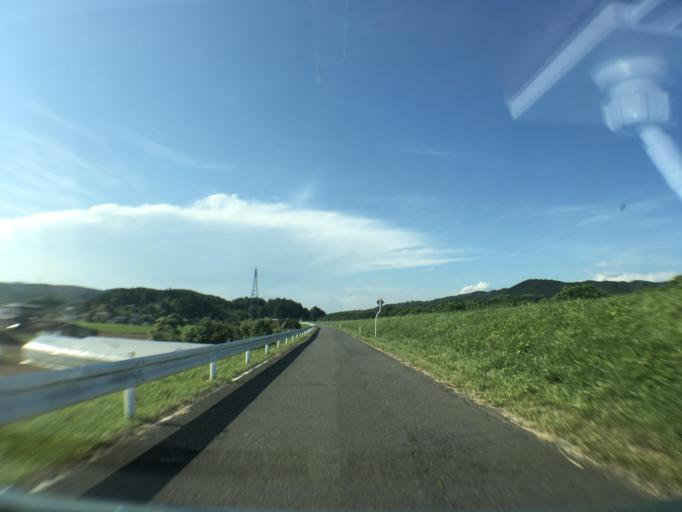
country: JP
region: Miyagi
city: Wakuya
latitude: 38.6143
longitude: 141.2937
